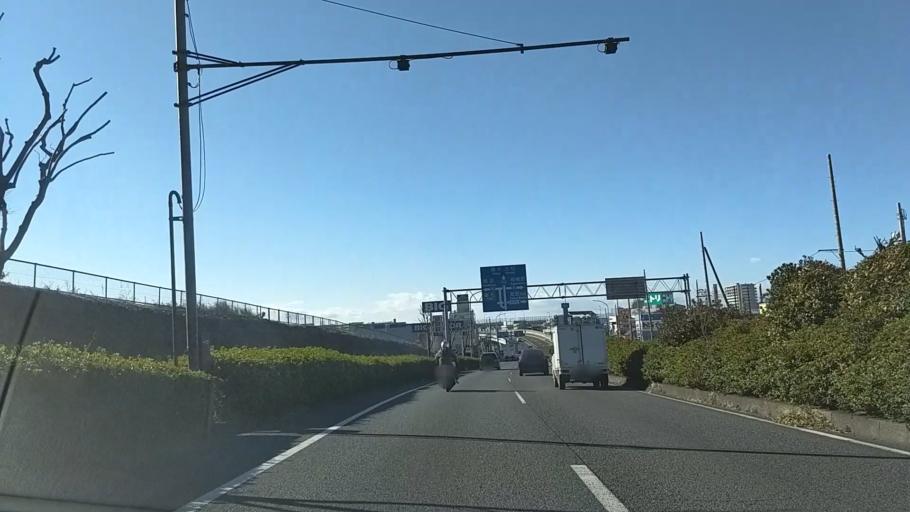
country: JP
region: Tokyo
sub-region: Machida-shi
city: Machida
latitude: 35.5143
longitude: 139.4805
